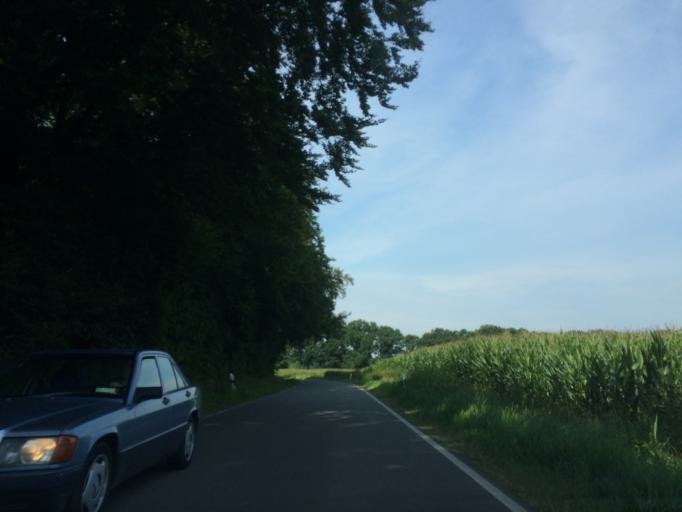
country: DE
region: Schleswig-Holstein
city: Altenhof
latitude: 54.4325
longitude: 9.8903
